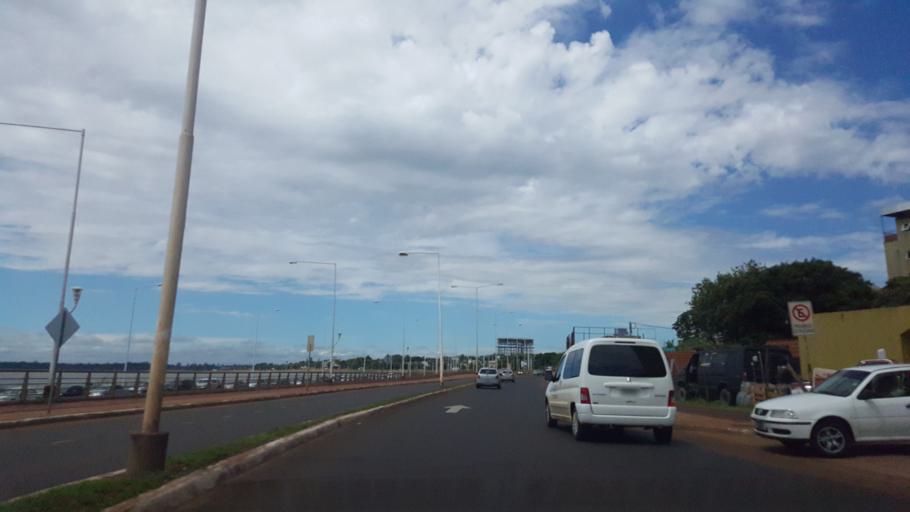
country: AR
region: Misiones
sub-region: Departamento de Capital
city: Posadas
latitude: -27.3880
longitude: -55.8891
